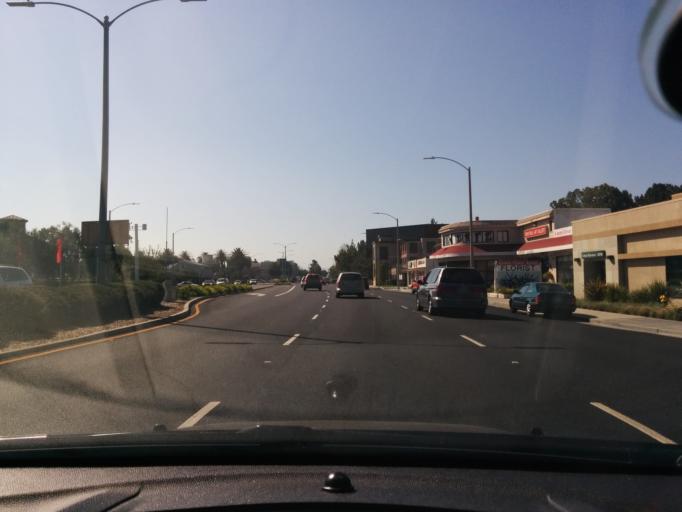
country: US
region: California
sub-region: Santa Clara County
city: Sunnyvale
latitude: 37.3686
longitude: -122.0339
